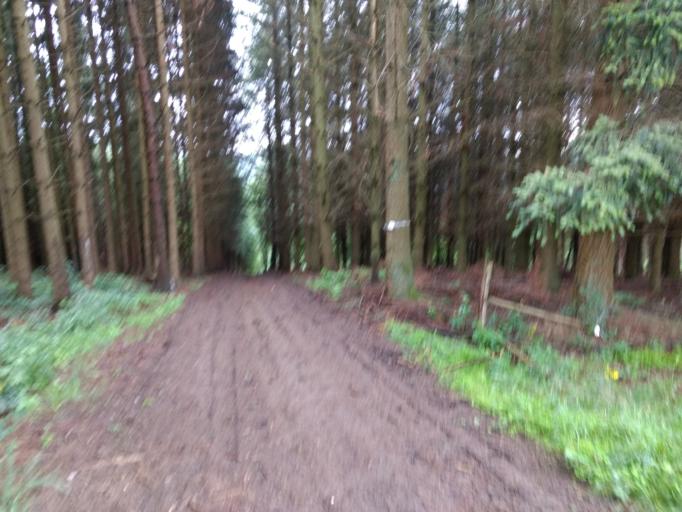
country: BE
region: Wallonia
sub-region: Province du Luxembourg
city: Bertogne
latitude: 50.1379
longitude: 5.7061
